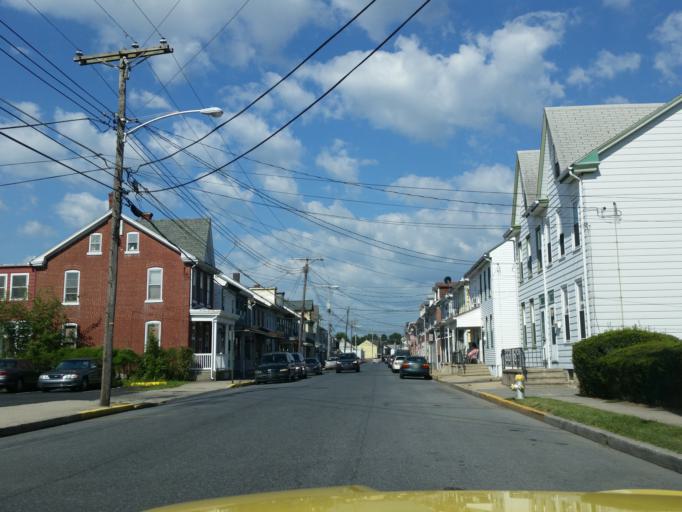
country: US
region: Pennsylvania
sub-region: Lebanon County
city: Lebanon
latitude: 40.3492
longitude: -76.4162
